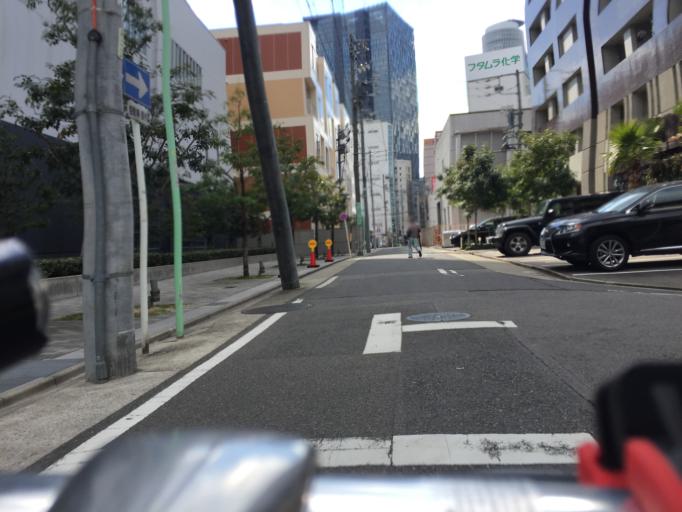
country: JP
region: Aichi
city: Nagoya-shi
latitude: 35.1763
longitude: 136.8847
